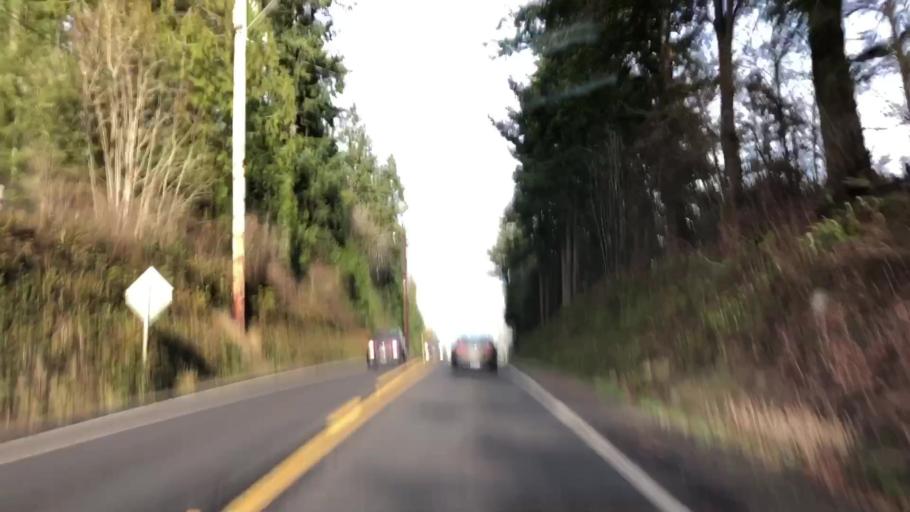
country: US
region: Washington
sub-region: Kitsap County
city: Kingston
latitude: 47.7919
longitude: -122.5415
